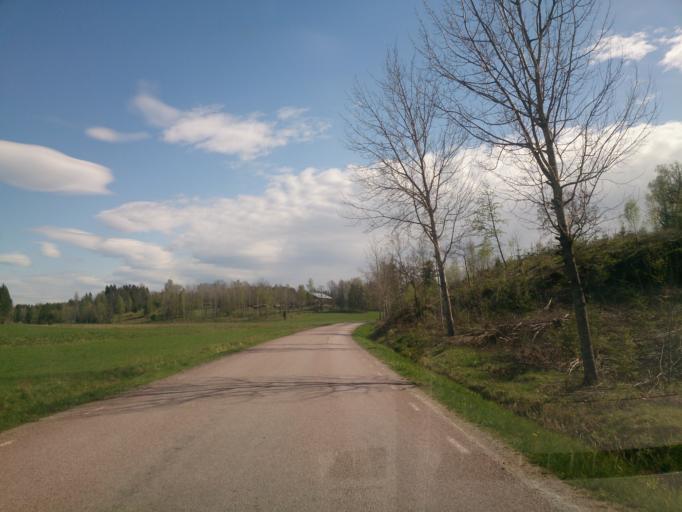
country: SE
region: OEstergoetland
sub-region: Linkopings Kommun
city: Ljungsbro
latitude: 58.5460
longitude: 15.5250
